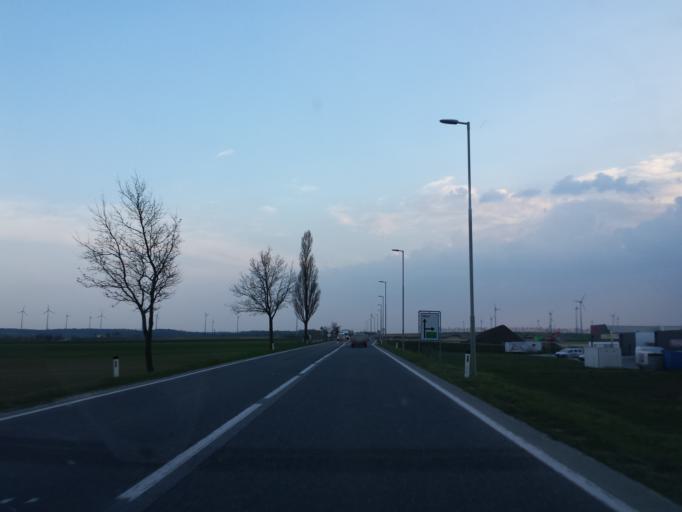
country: AT
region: Lower Austria
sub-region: Politischer Bezirk Mistelbach
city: Wilfersdorf
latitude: 48.5685
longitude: 16.6381
